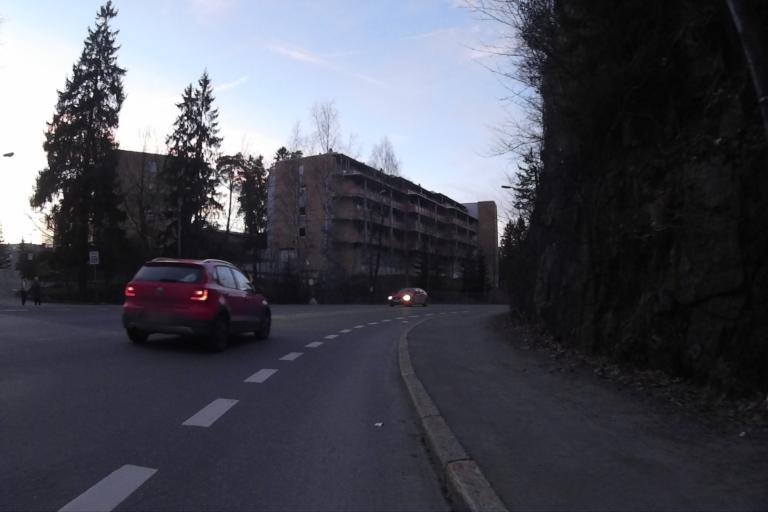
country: NO
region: Oslo
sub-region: Oslo
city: Oslo
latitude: 59.9013
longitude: 10.8251
